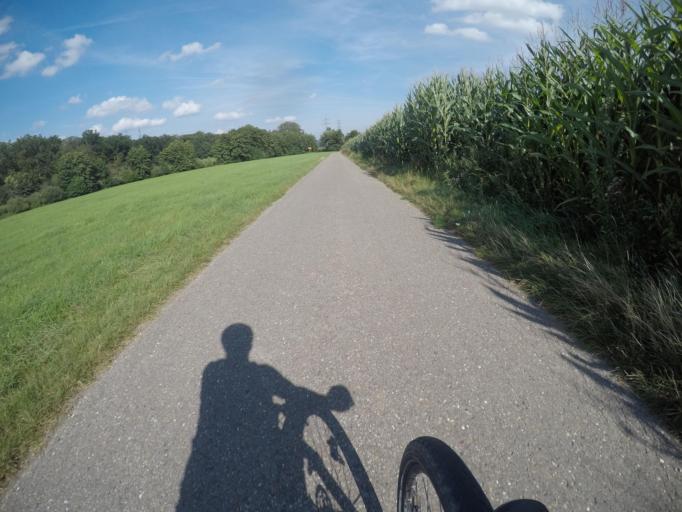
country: DE
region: Baden-Wuerttemberg
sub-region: Karlsruhe Region
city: Olbronn-Durrn
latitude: 48.9641
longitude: 8.7535
